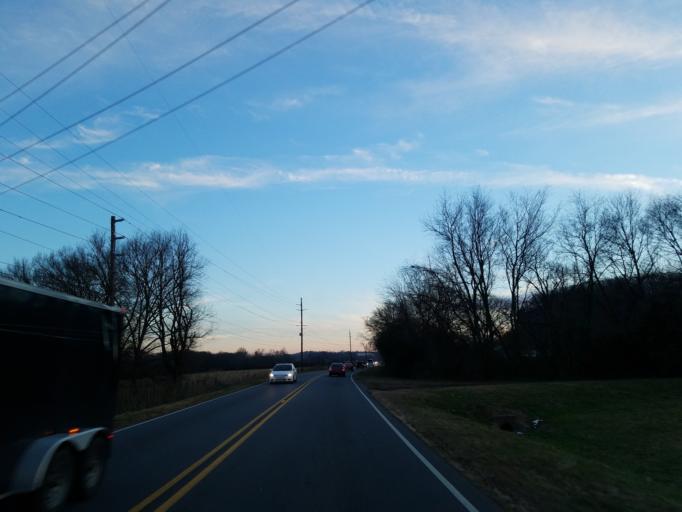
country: US
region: Georgia
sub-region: Bartow County
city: Cartersville
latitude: 34.1620
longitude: -84.8289
